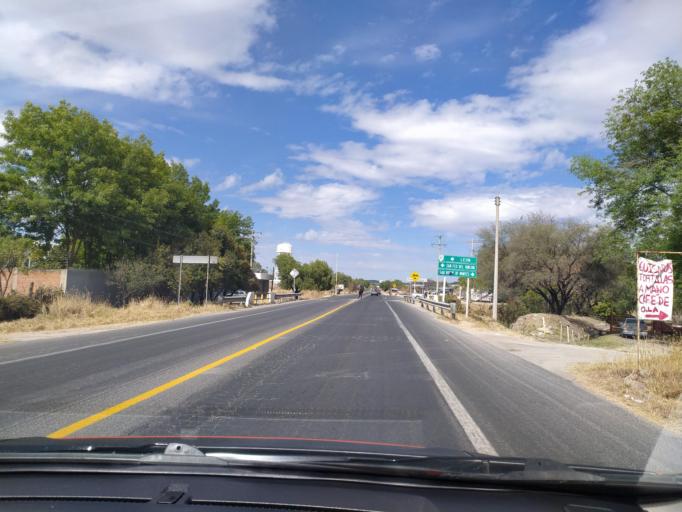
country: LA
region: Oudomxai
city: Muang La
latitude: 21.0199
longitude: 101.8266
